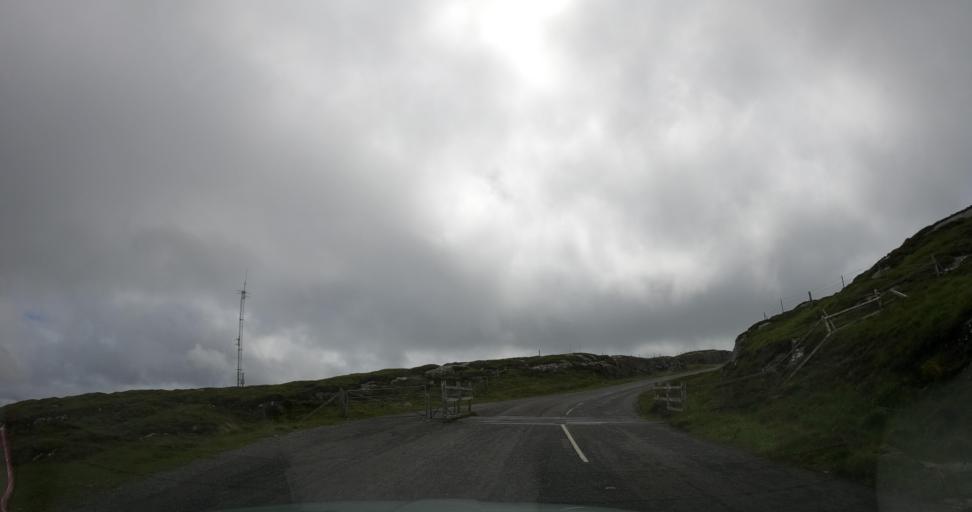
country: GB
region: Scotland
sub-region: Eilean Siar
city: Barra
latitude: 56.9513
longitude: -7.5097
